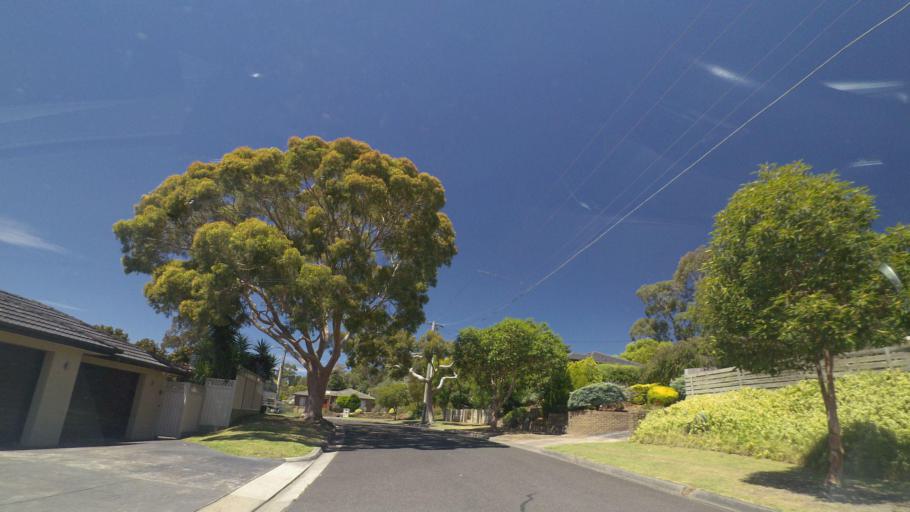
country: AU
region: Victoria
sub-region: Maroondah
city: Croydon North
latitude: -37.7791
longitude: 145.3164
